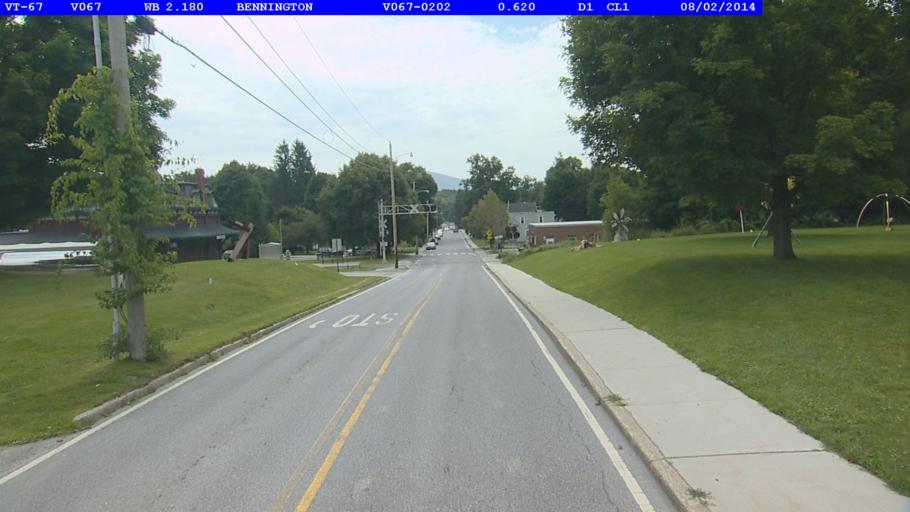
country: US
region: Vermont
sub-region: Bennington County
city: North Bennington
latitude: 42.9329
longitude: -73.2427
